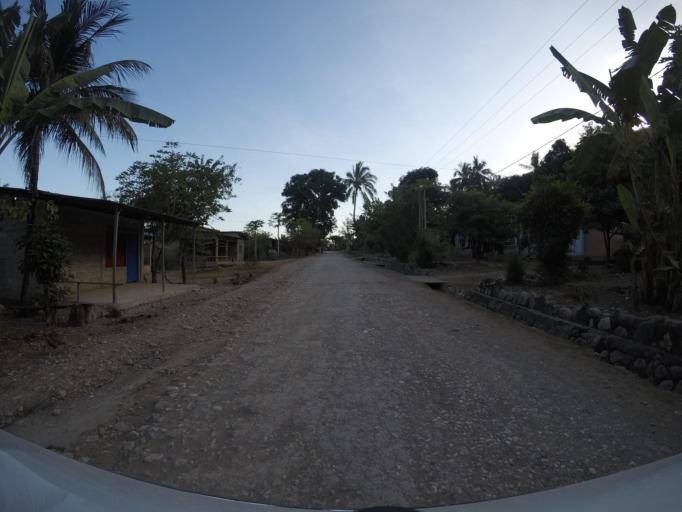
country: TL
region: Viqueque
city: Viqueque
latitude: -8.7968
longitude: 126.5561
